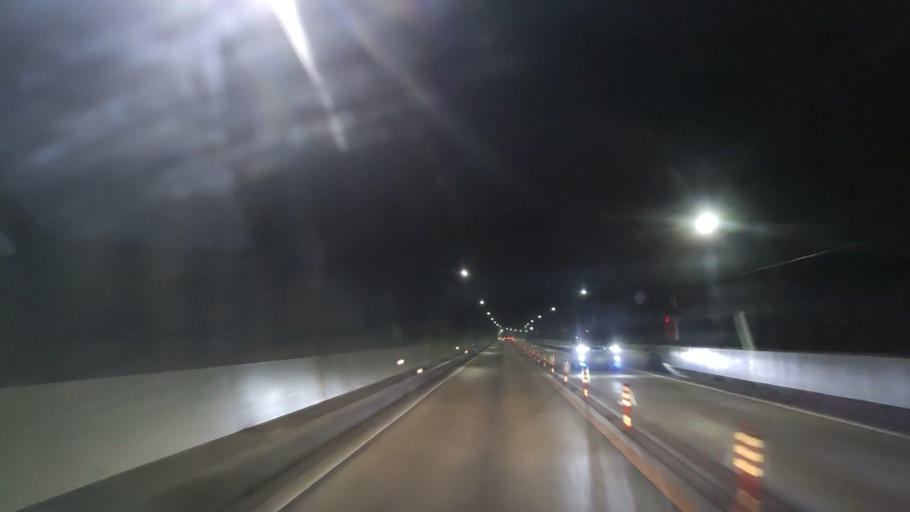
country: JP
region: Hiroshima
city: Innoshima
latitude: 34.1794
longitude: 133.0683
